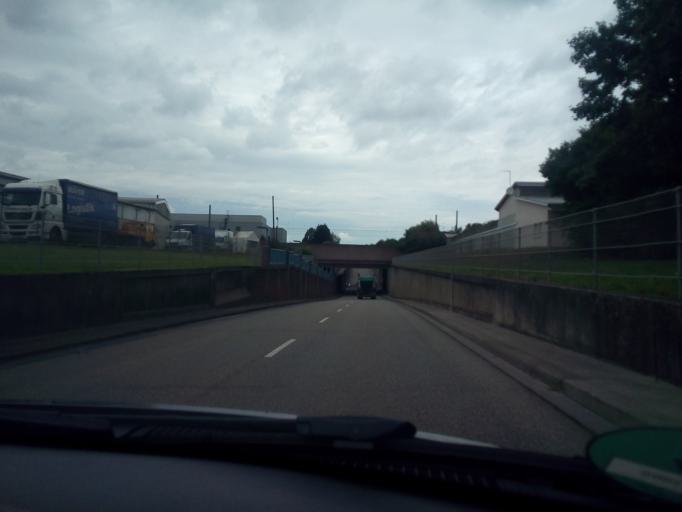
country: DE
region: Baden-Wuerttemberg
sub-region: Karlsruhe Region
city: Ottersweier
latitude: 48.6763
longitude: 8.1118
